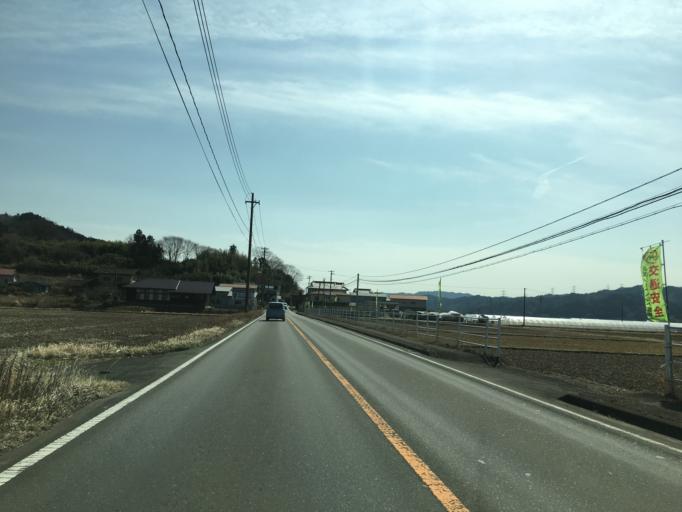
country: JP
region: Ibaraki
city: Daigo
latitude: 36.9182
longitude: 140.4164
